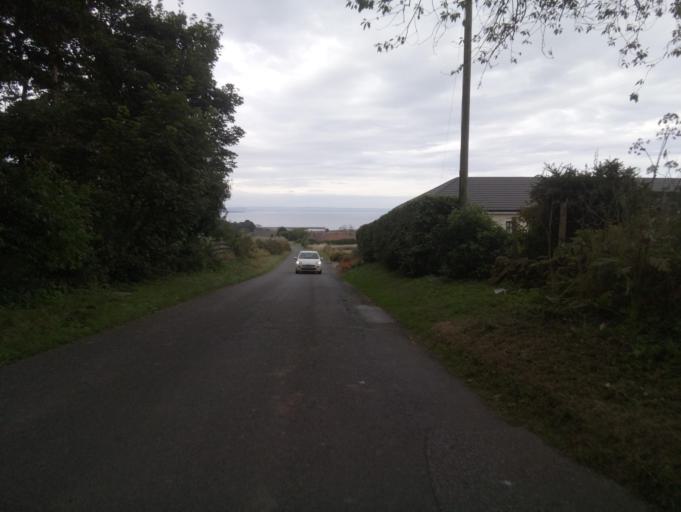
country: GB
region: Scotland
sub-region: Fife
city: Saint Andrews
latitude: 56.3185
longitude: -2.7799
